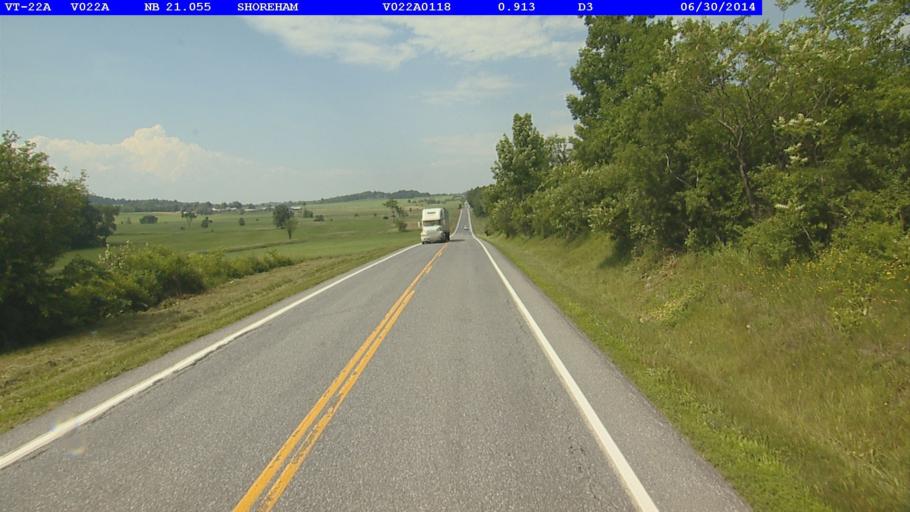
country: US
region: New York
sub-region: Essex County
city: Ticonderoga
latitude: 43.8626
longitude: -73.3096
